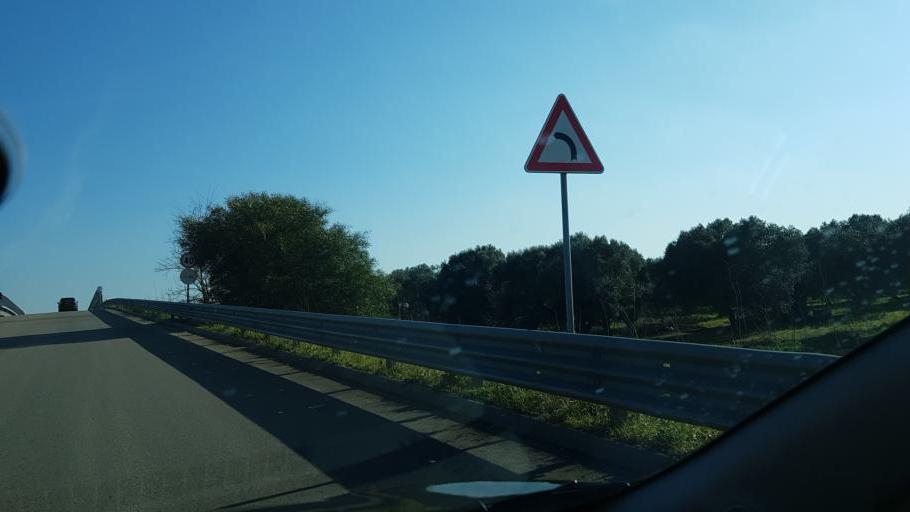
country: IT
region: Apulia
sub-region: Provincia di Brindisi
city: Mesagne
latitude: 40.5763
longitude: 17.8320
